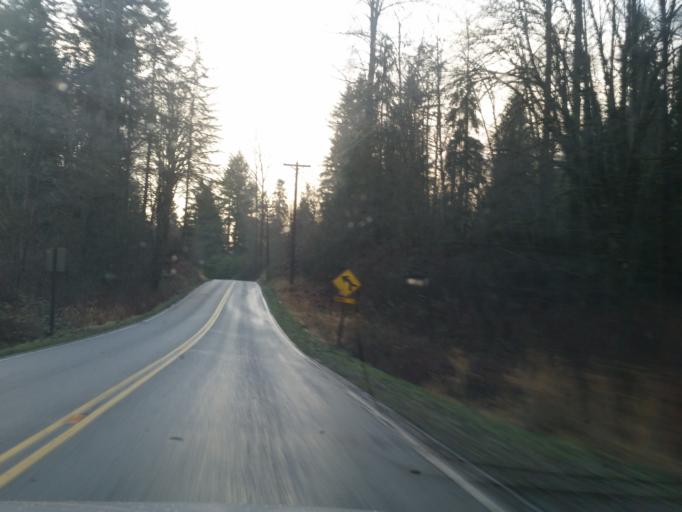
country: US
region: Washington
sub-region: Snohomish County
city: Maltby
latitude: 47.8145
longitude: -122.0942
